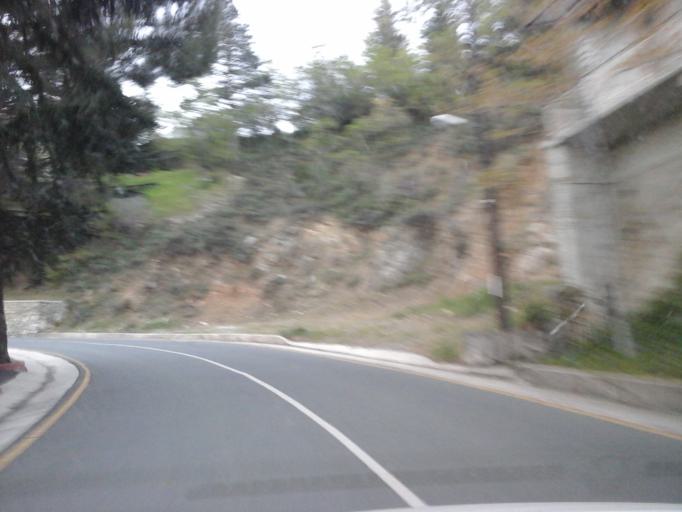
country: CY
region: Lefkosia
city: Kakopetria
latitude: 34.9696
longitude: 32.8260
